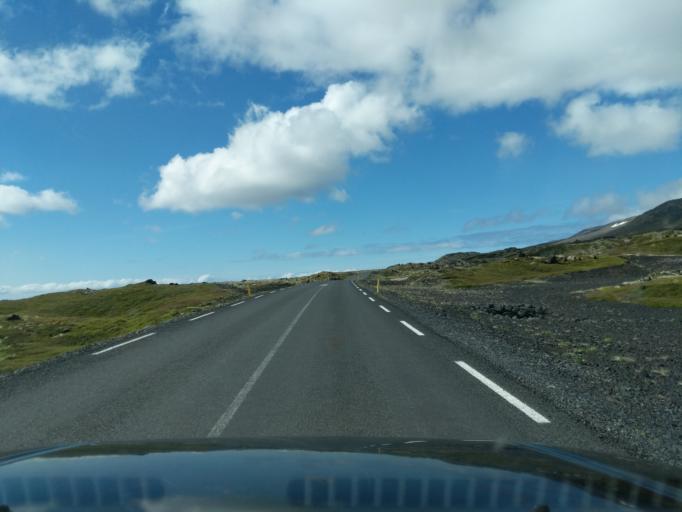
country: IS
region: West
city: Olafsvik
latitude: 64.7660
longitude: -23.8686
